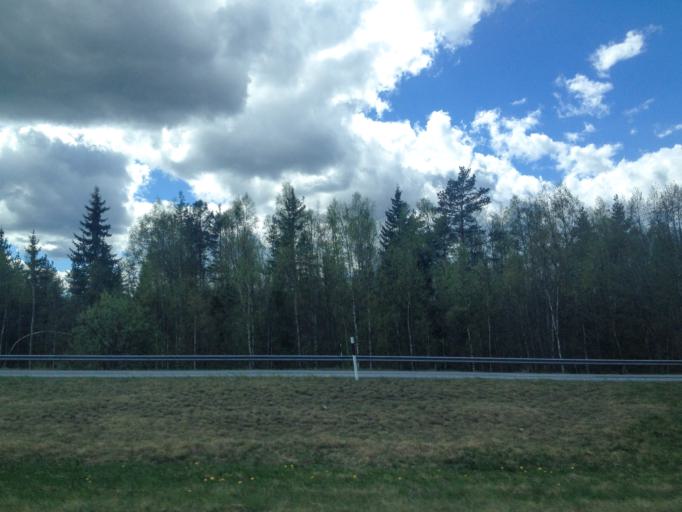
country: FI
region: Haeme
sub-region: Haemeenlinna
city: Kalvola
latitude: 61.1281
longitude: 24.1110
